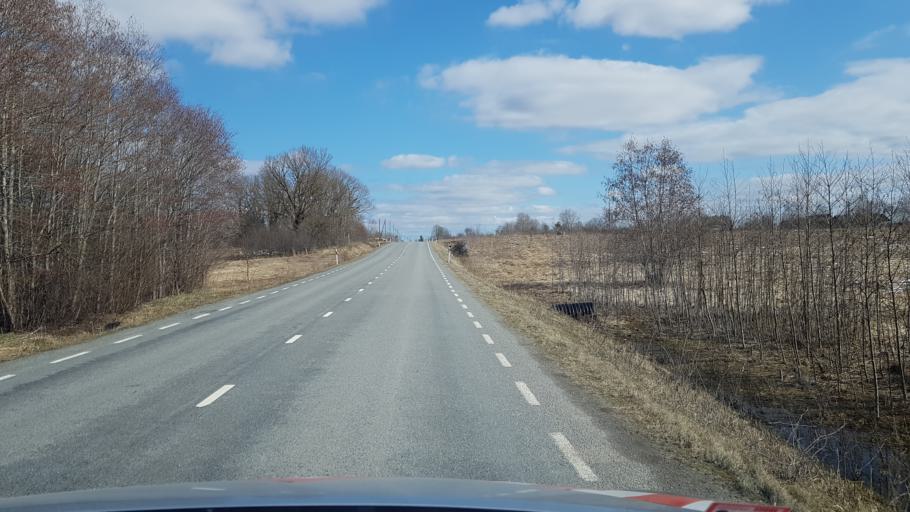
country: EE
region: Laeaene-Virumaa
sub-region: Tapa vald
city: Tapa
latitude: 59.2689
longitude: 25.9423
